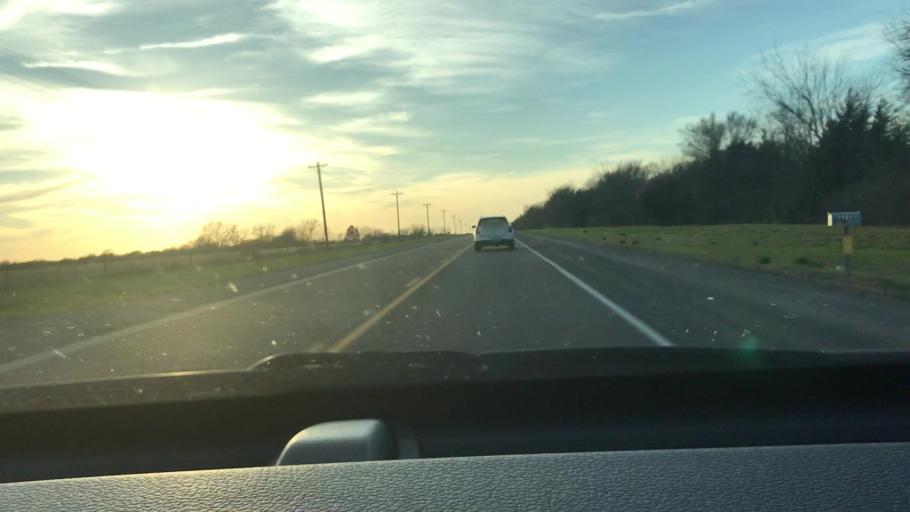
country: US
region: Texas
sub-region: Red River County
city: Clarksville
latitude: 33.6038
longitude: -94.9904
